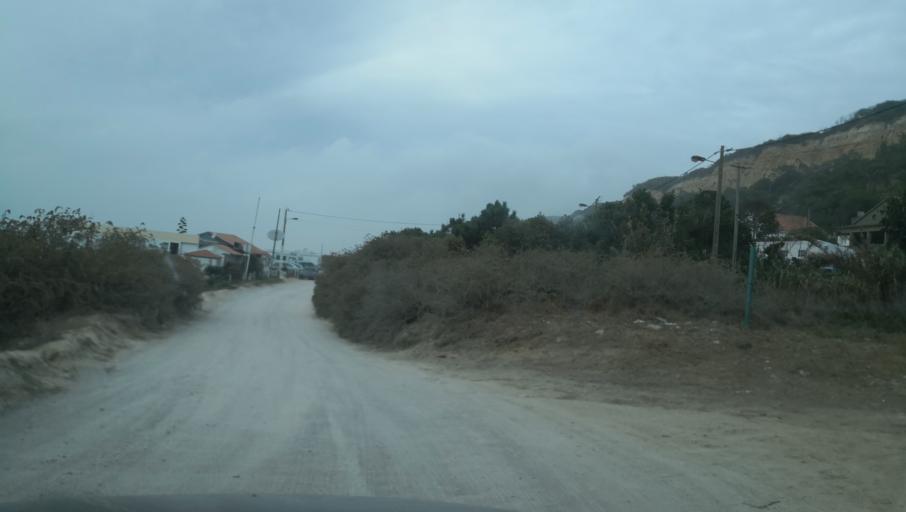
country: PT
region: Setubal
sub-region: Almada
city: Charneca
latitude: 38.5660
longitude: -9.1925
